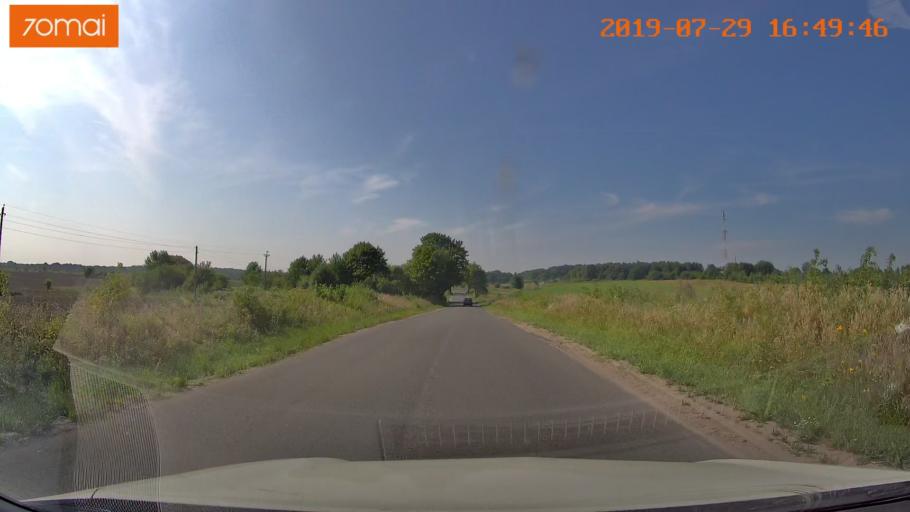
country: RU
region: Kaliningrad
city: Primorsk
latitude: 54.7972
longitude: 20.0617
